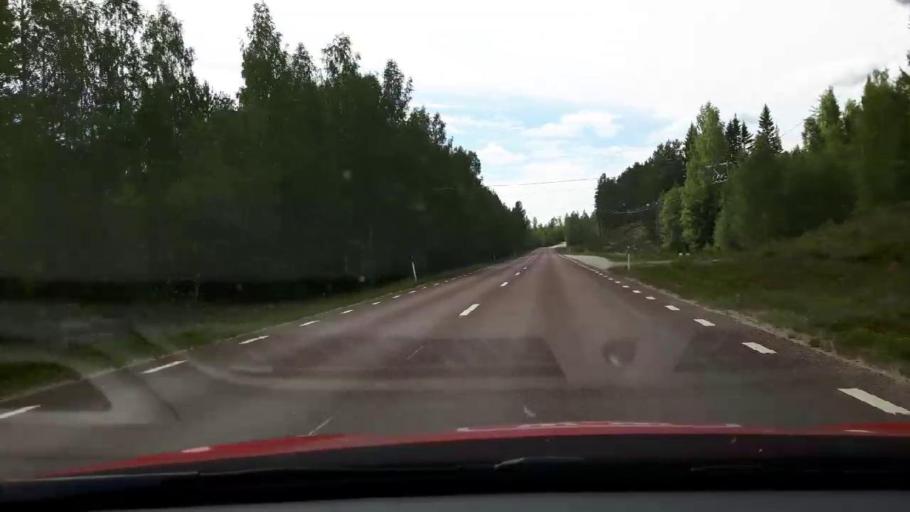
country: SE
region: Jaemtland
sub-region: Harjedalens Kommun
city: Sveg
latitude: 62.0551
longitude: 14.9034
